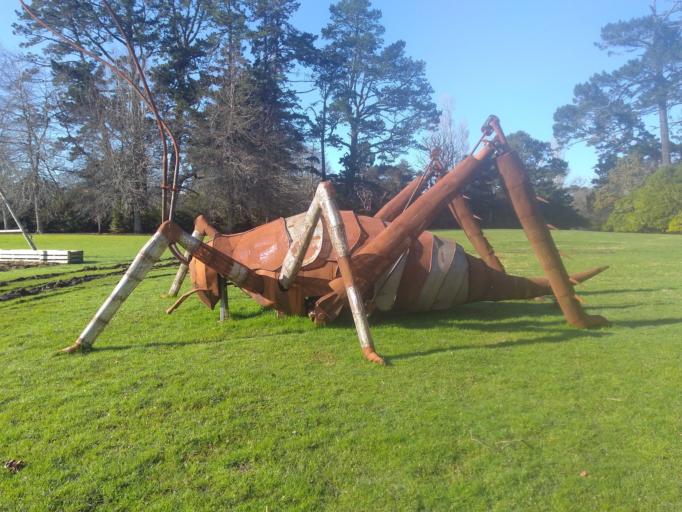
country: NZ
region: Auckland
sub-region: Auckland
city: Rosebank
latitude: -36.8780
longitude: 174.6281
